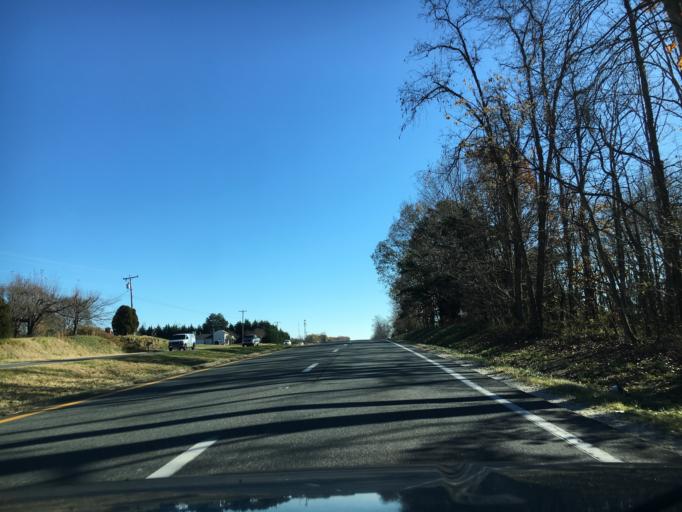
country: US
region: Virginia
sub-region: Appomattox County
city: Appomattox
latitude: 37.3587
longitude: -78.8963
